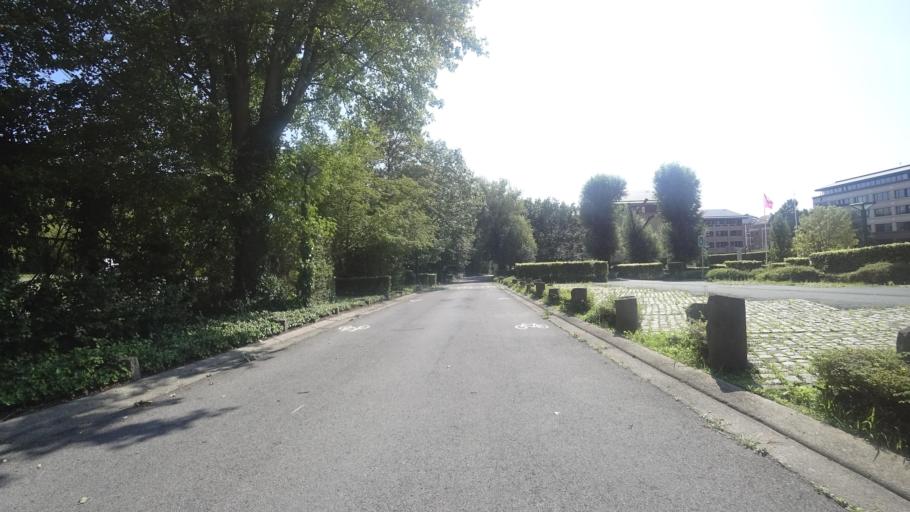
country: BE
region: Flanders
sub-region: Provincie Vlaams-Brabant
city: Kraainem
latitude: 50.8580
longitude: 4.4302
